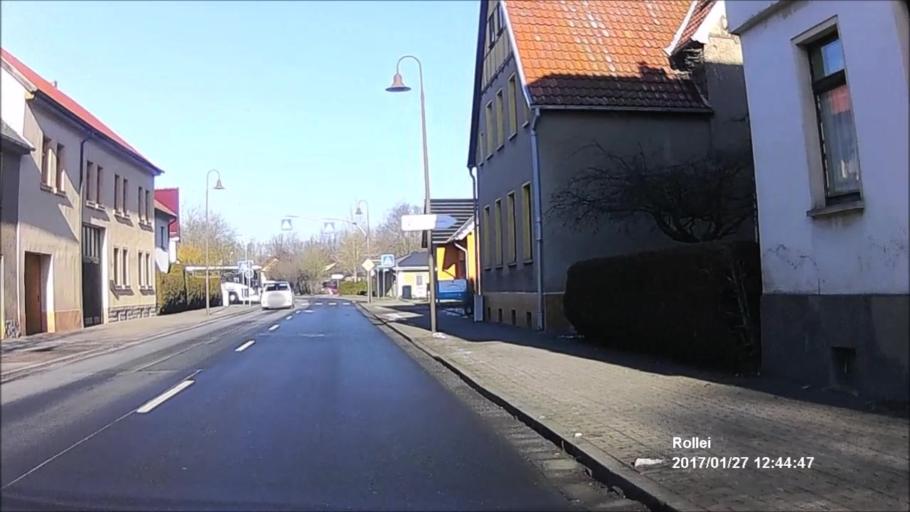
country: DE
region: Thuringia
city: Bad Tennstedt
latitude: 51.1555
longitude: 10.8395
